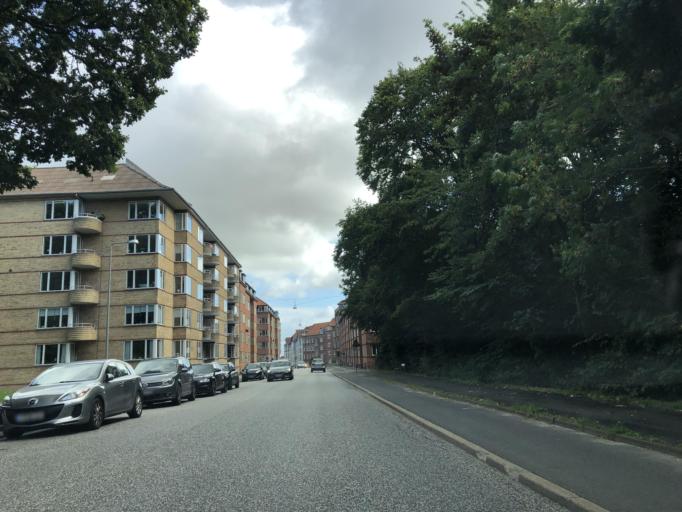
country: DK
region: Central Jutland
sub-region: Randers Kommune
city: Randers
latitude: 56.4655
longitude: 10.0250
